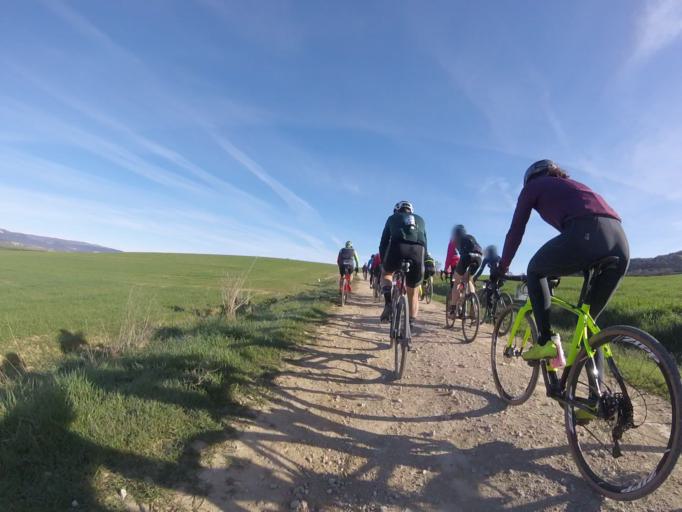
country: ES
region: Navarre
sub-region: Provincia de Navarra
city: Villatuerta
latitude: 42.6568
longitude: -1.9693
